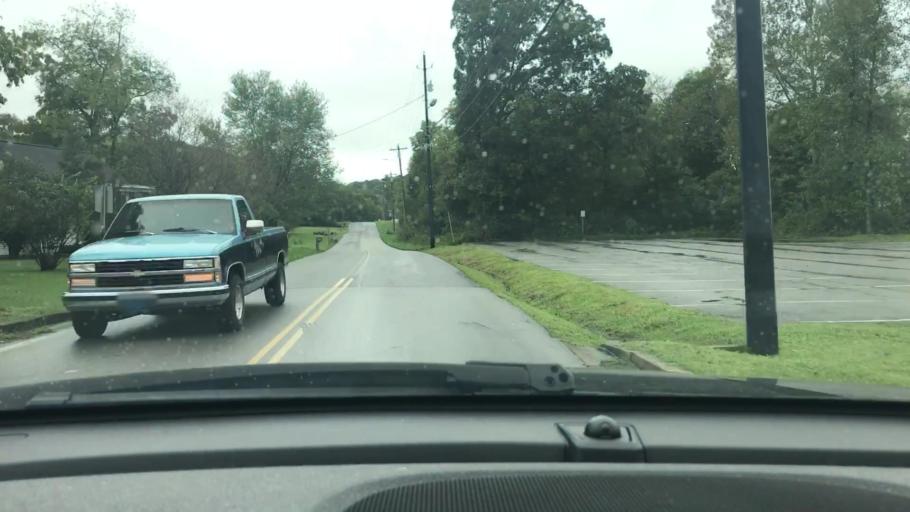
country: US
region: Tennessee
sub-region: Cheatham County
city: Kingston Springs
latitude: 36.1017
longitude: -87.1151
